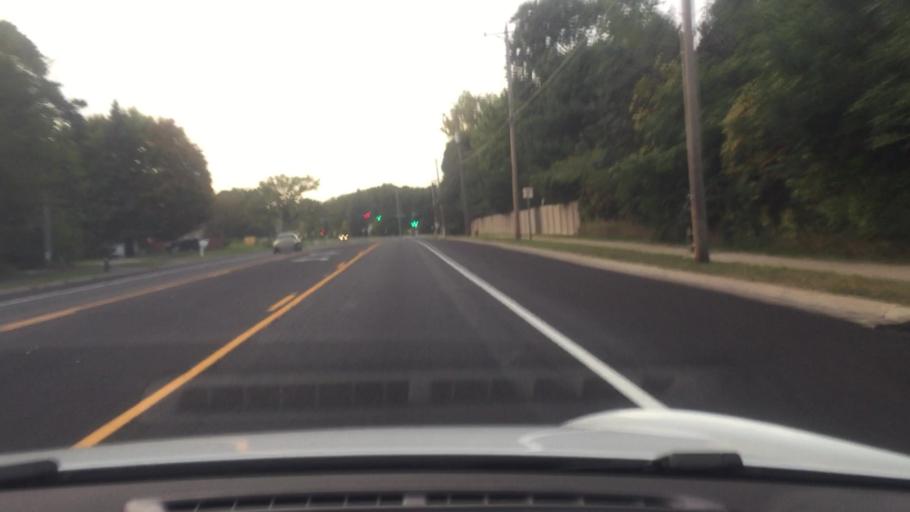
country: US
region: Minnesota
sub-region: Ramsey County
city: Shoreview
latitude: 45.0844
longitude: -93.1196
